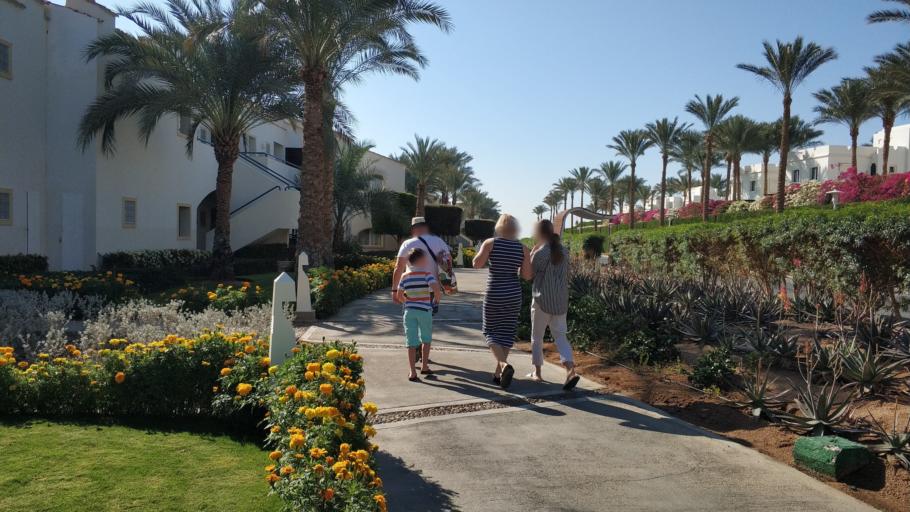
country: EG
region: South Sinai
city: Sharm el-Sheikh
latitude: 27.9188
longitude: 34.3604
